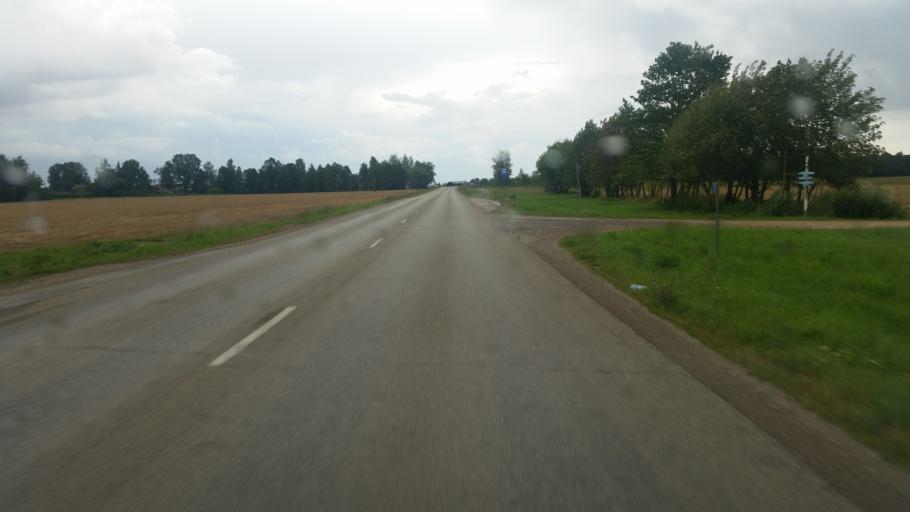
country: LV
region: Bauskas Rajons
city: Bauska
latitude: 56.4239
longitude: 24.2222
